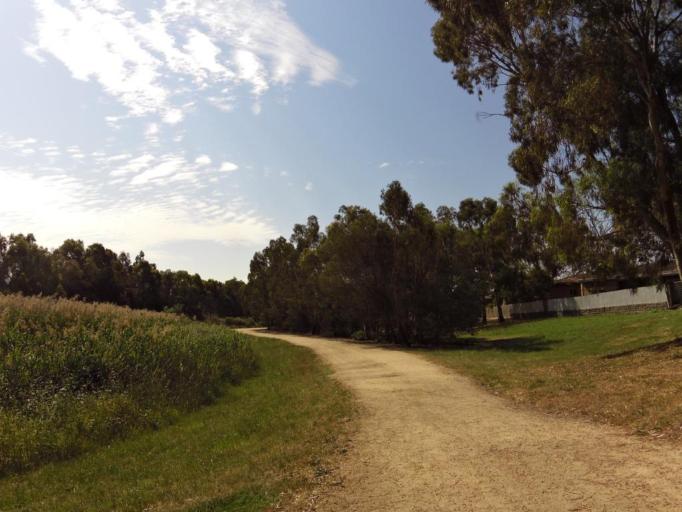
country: AU
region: Victoria
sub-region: Whittlesea
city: Epping
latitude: -37.6469
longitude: 145.0330
